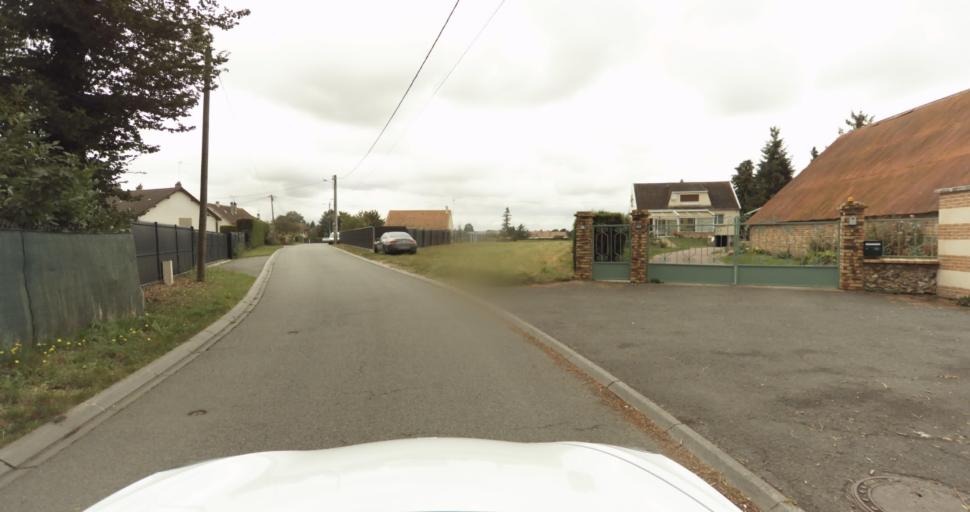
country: FR
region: Haute-Normandie
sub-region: Departement de l'Eure
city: Saint-Sebastien-de-Morsent
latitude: 49.0068
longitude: 1.0664
